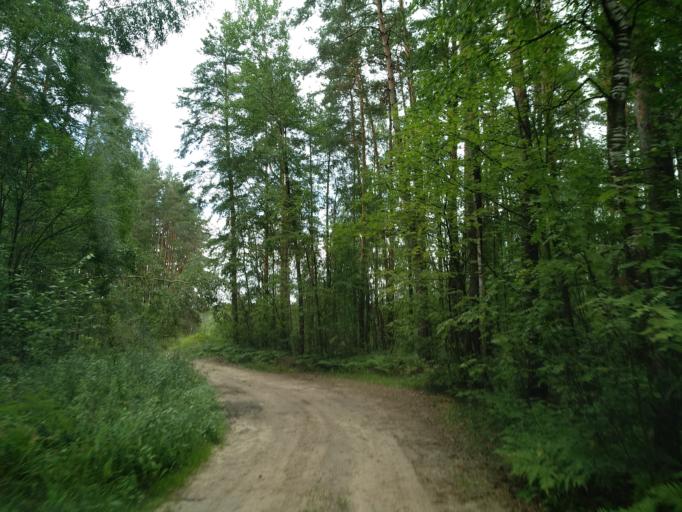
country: RU
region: Moskovskaya
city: Krasnyy Tkach
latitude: 55.3806
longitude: 39.2356
